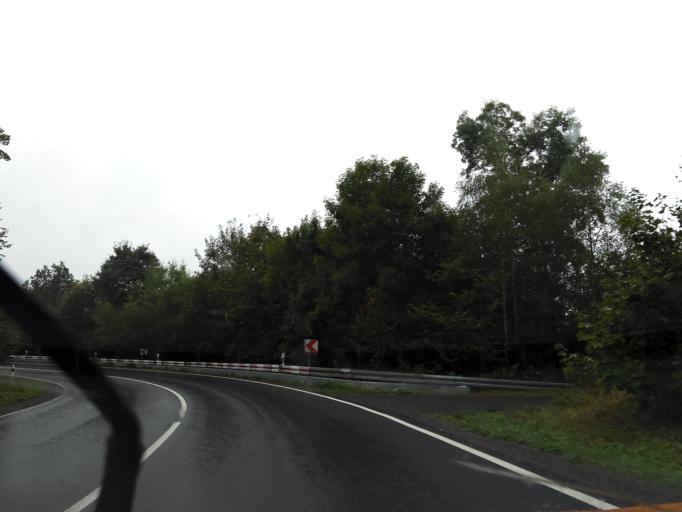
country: DE
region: Saxony-Anhalt
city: Friedrichsbrunn
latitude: 51.6501
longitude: 11.0723
